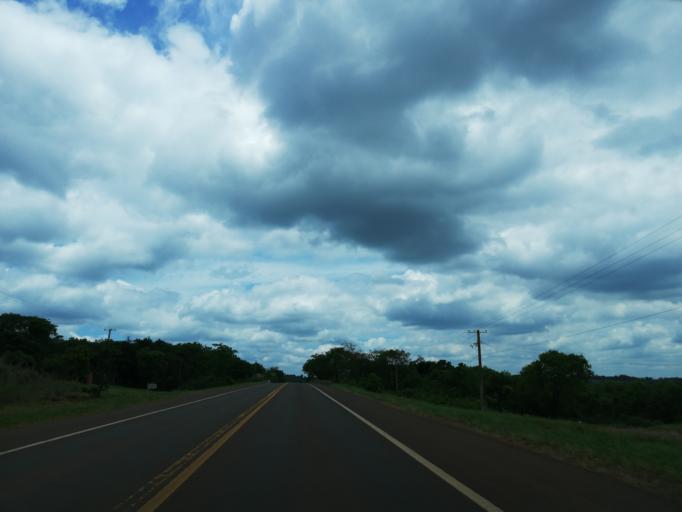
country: AR
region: Misiones
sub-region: Departamento de Leandro N. Alem
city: Leandro N. Alem
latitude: -27.6325
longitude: -55.3427
